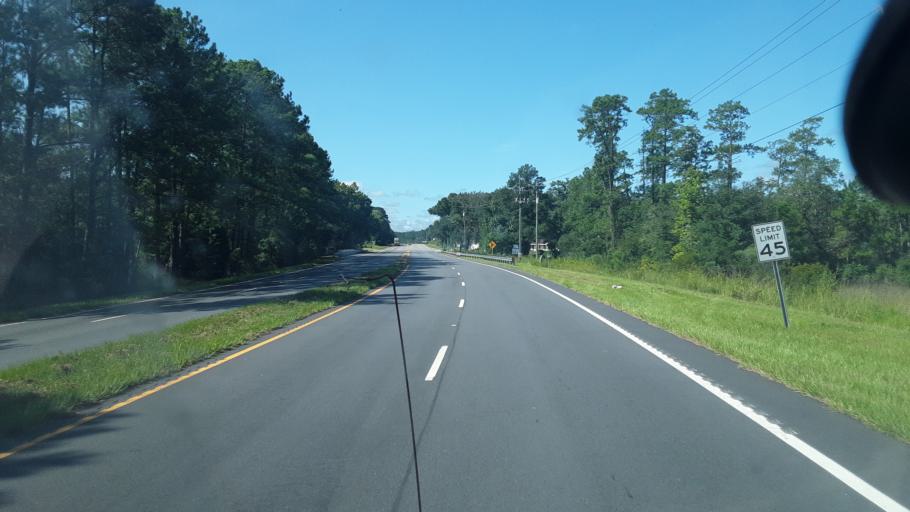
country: US
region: South Carolina
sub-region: Jasper County
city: Ridgeland
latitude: 32.5905
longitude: -80.9255
